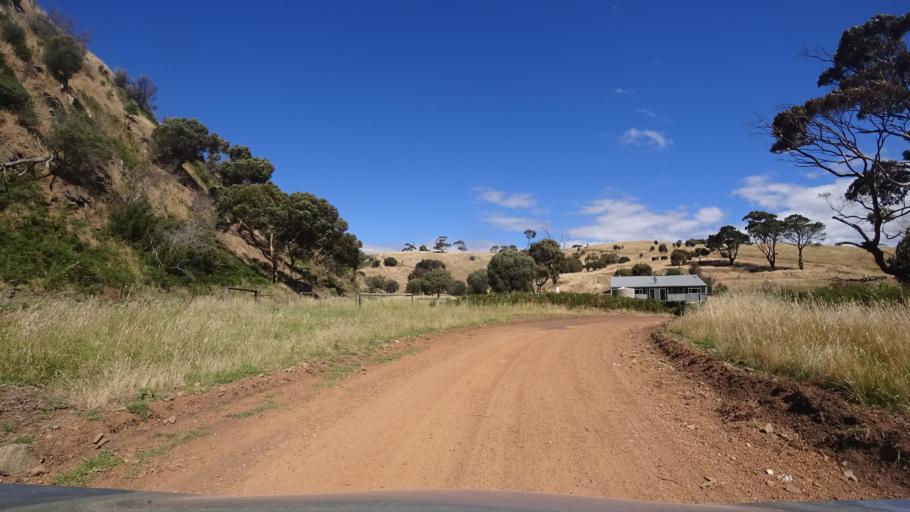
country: AU
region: South Australia
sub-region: Kangaroo Island
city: Kingscote
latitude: -35.6806
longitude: 136.9723
